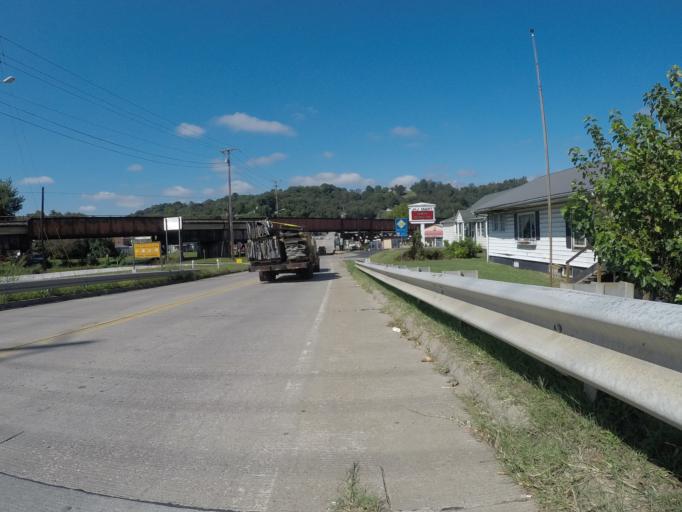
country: US
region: Kentucky
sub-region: Boyd County
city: Catlettsburg
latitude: 38.4047
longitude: -82.5978
